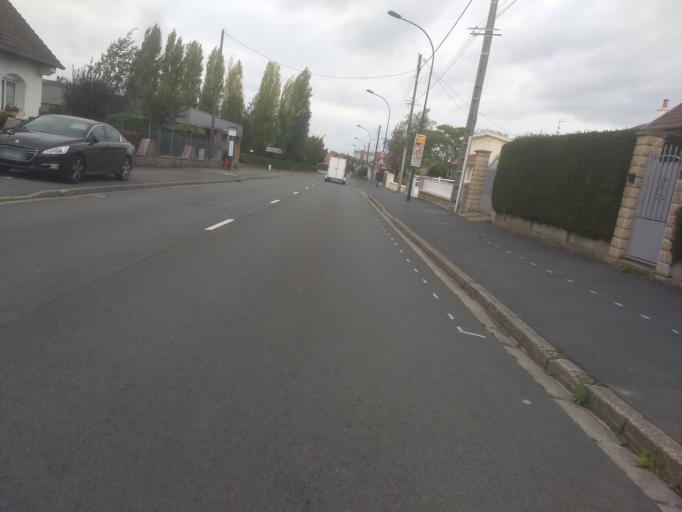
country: FR
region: Nord-Pas-de-Calais
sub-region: Departement du Pas-de-Calais
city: Beaurains
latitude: 50.2677
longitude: 2.7764
